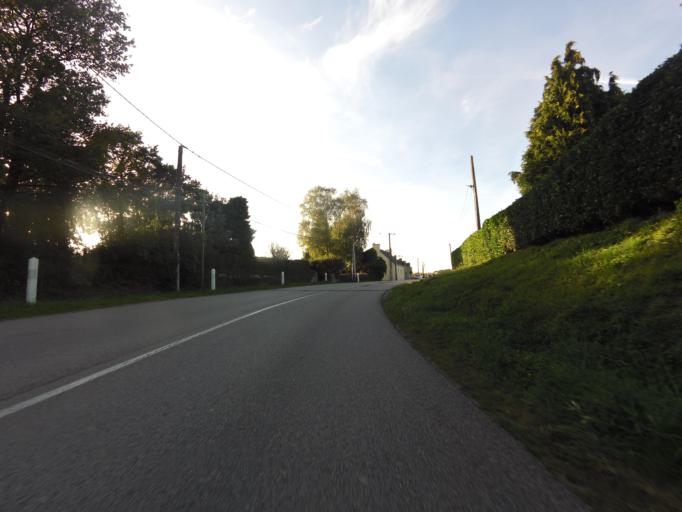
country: FR
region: Brittany
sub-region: Departement du Morbihan
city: Questembert
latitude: 47.6626
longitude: -2.4749
